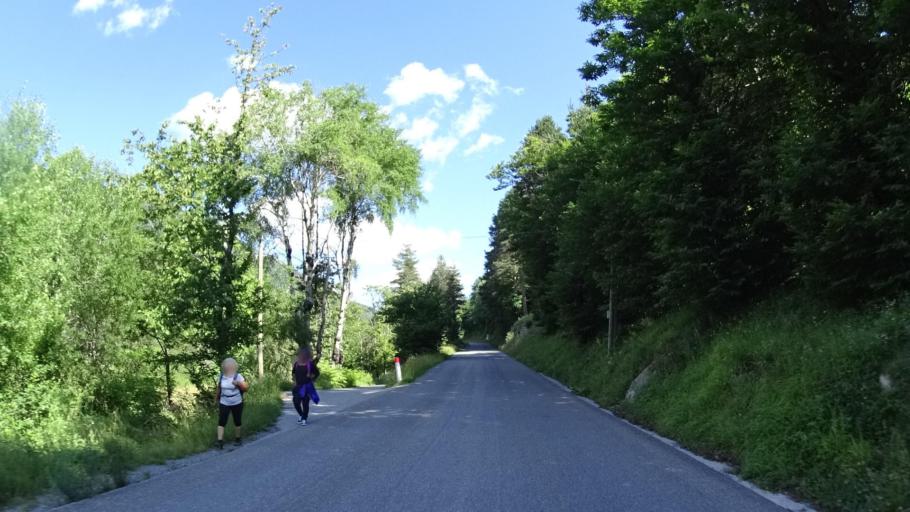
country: FR
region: Provence-Alpes-Cote d'Azur
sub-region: Departement des Alpes-de-Haute-Provence
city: Annot
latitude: 43.9749
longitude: 6.6536
